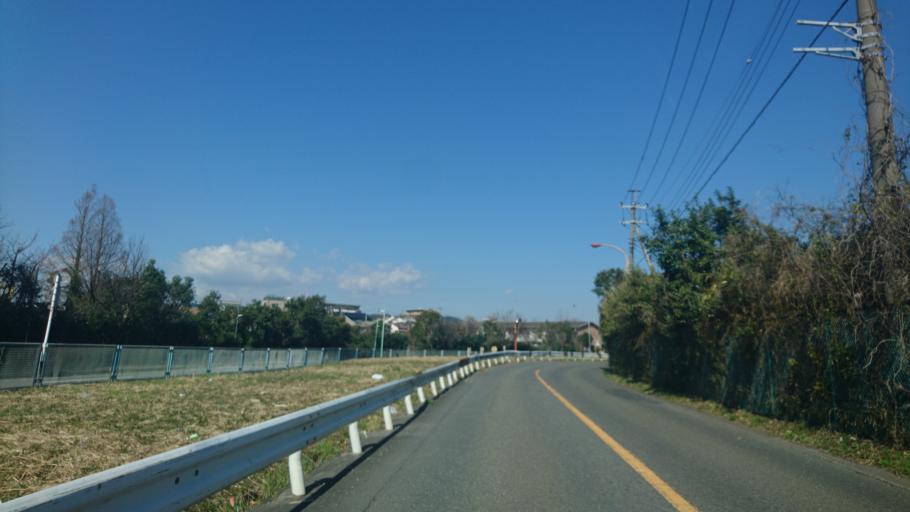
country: JP
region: Kanagawa
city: Fujisawa
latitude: 35.3972
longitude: 139.4481
